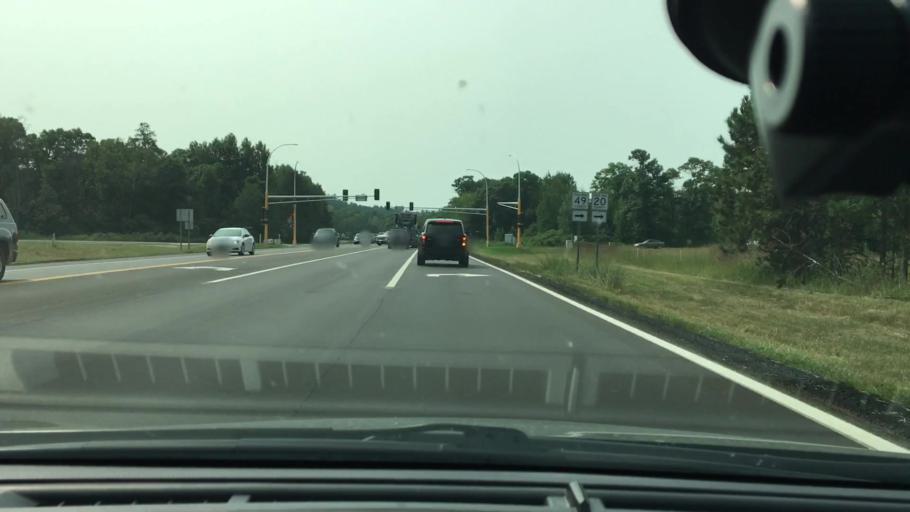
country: US
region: Minnesota
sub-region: Crow Wing County
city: Brainerd
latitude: 46.3998
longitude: -94.1769
